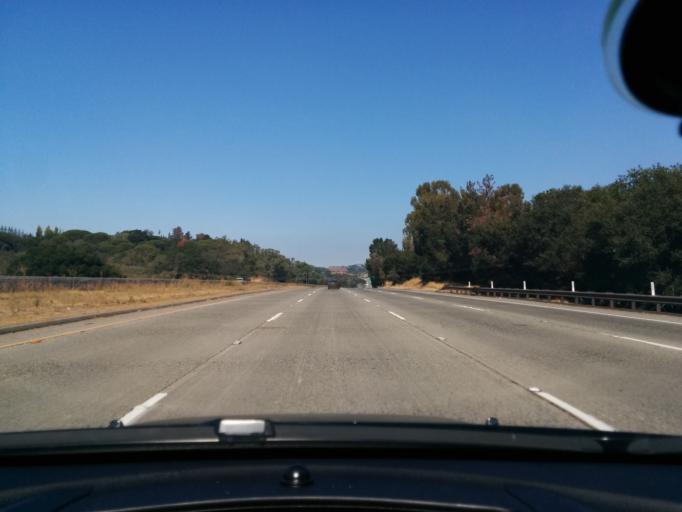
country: US
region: California
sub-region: San Mateo County
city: Woodside
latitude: 37.4299
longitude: -122.2363
